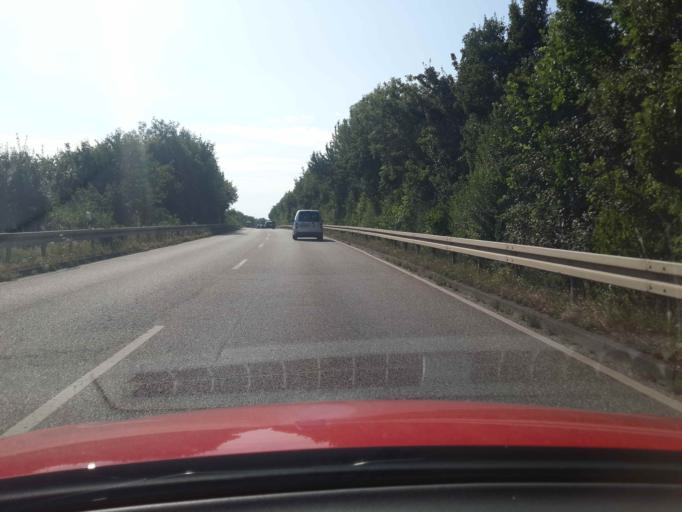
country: DE
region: Baden-Wuerttemberg
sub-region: Regierungsbezirk Stuttgart
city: Leingarten
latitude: 49.1474
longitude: 9.1307
